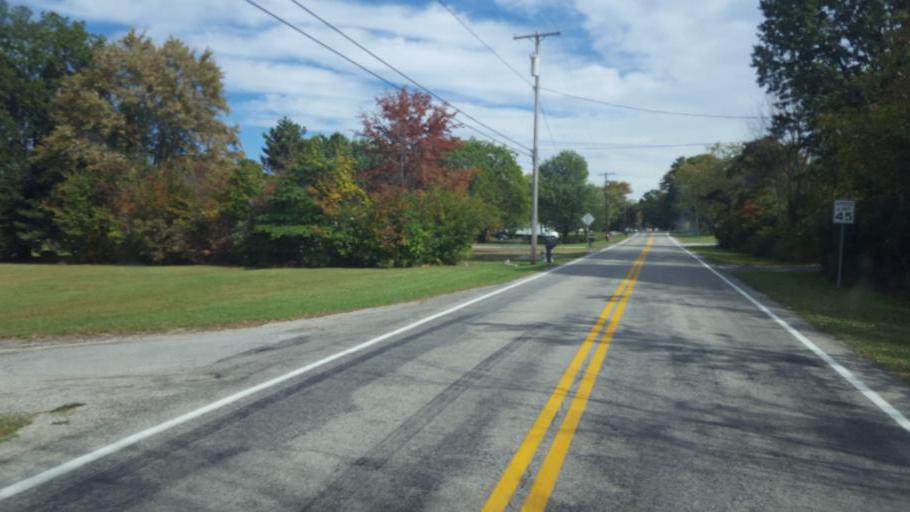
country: US
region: Ohio
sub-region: Lorain County
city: Vermilion
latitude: 41.3882
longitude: -82.3637
